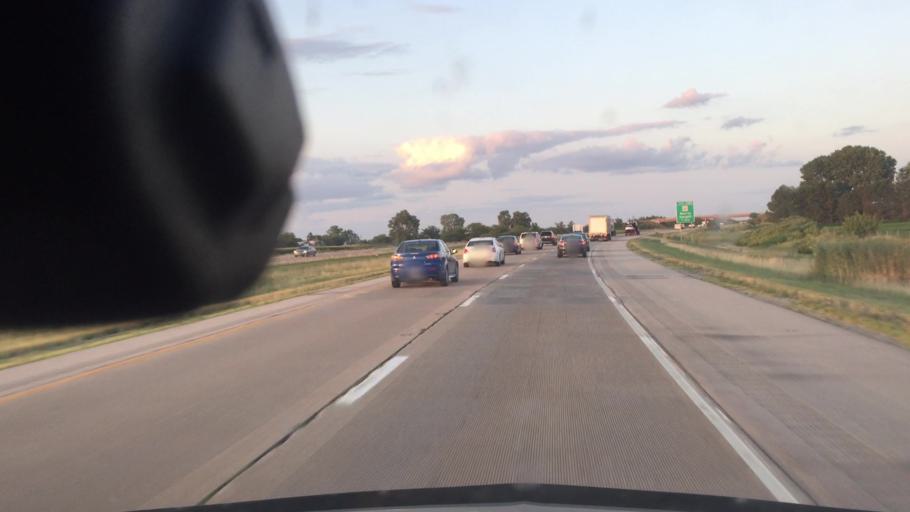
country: US
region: Illinois
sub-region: Livingston County
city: Dwight
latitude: 41.1121
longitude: -88.4406
